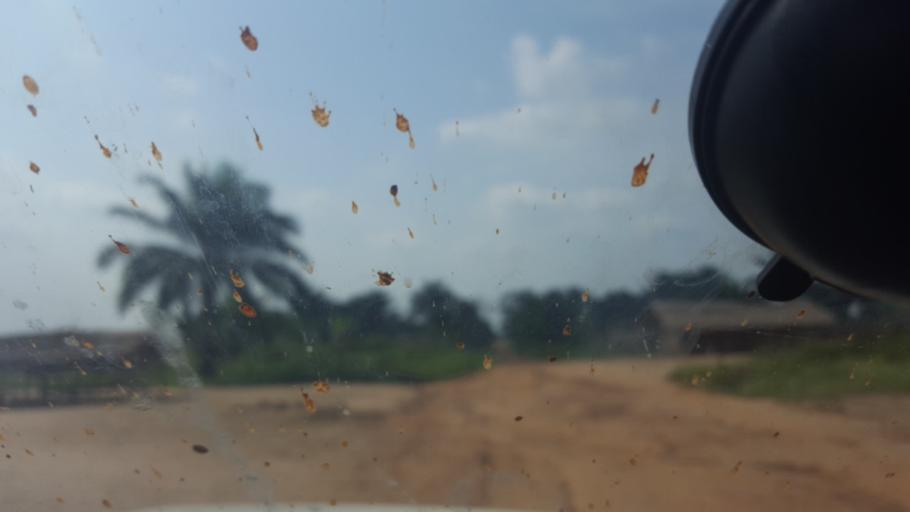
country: CD
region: Bandundu
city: Bandundu
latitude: -3.7526
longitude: 17.0392
